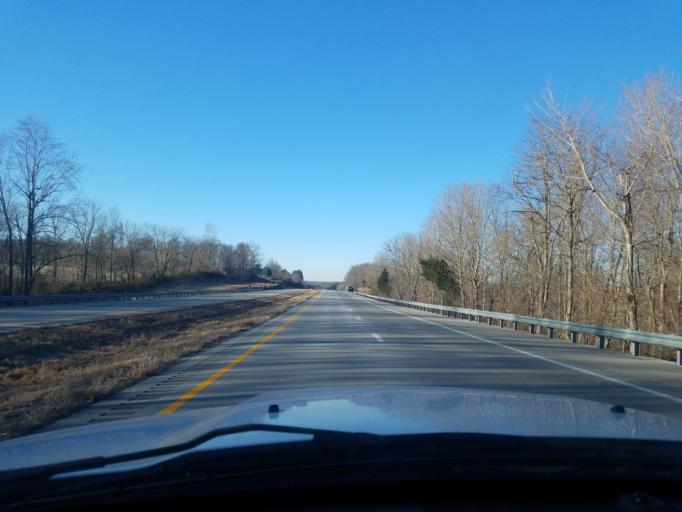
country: US
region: Kentucky
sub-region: Grayson County
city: Leitchfield
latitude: 37.4403
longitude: -86.3714
